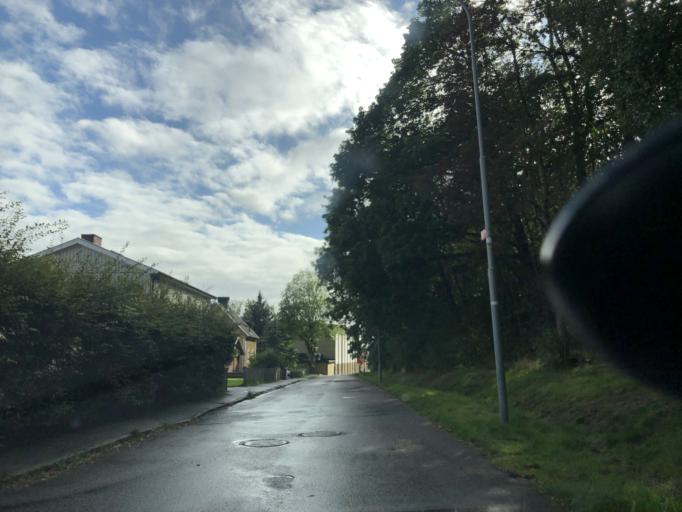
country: SE
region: Vaestra Goetaland
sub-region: Goteborg
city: Goeteborg
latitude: 57.7321
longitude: 11.9693
